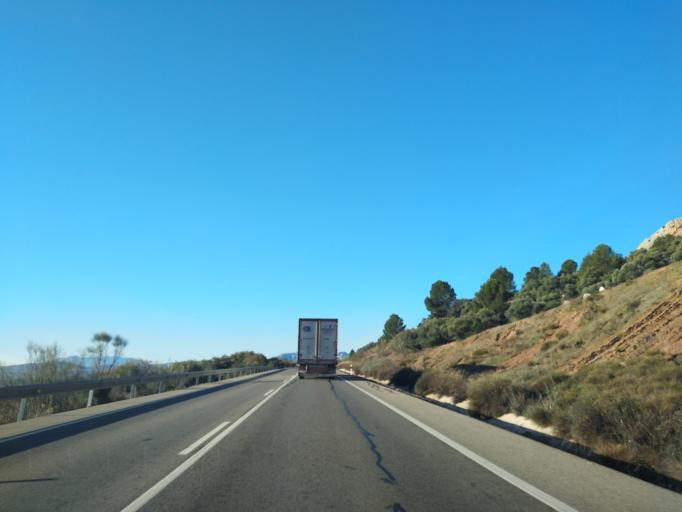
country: ES
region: Andalusia
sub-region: Provincia de Malaga
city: Campillos
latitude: 36.9719
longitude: -4.8385
